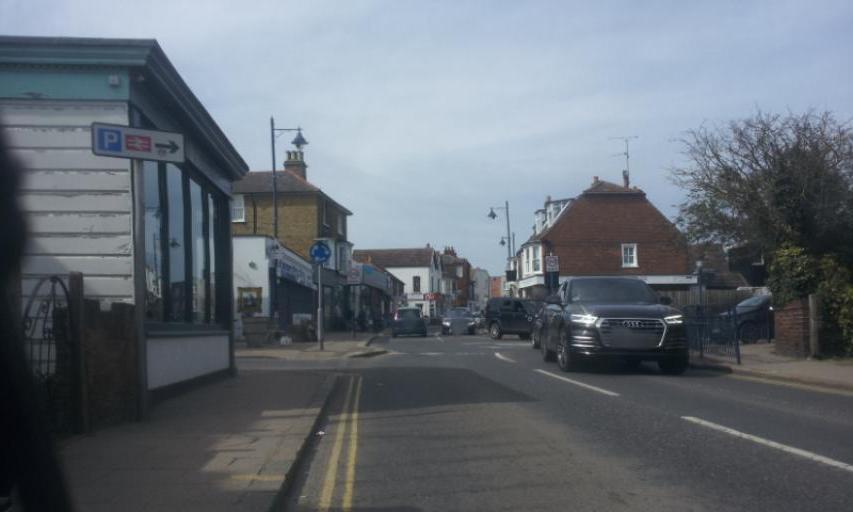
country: GB
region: England
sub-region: Kent
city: Whitstable
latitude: 51.3549
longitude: 1.0253
